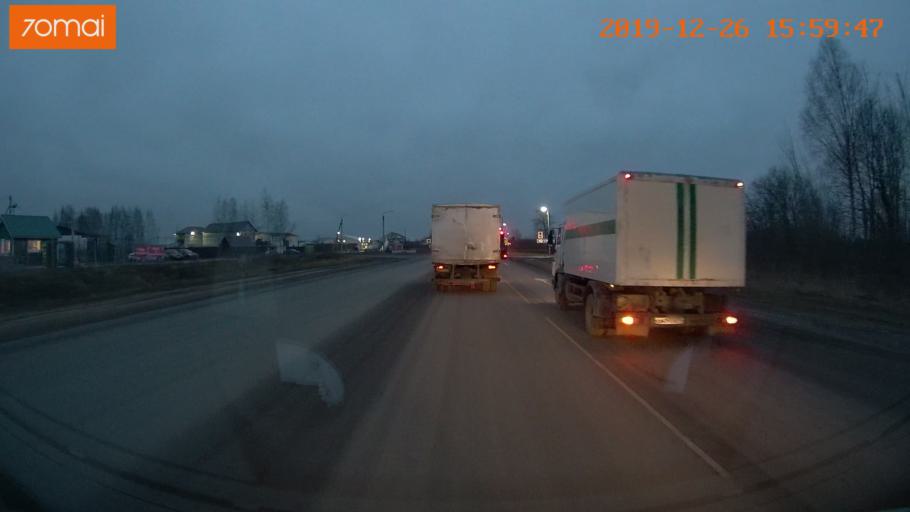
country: RU
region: Jaroslavl
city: Rybinsk
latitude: 58.0293
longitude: 38.8044
